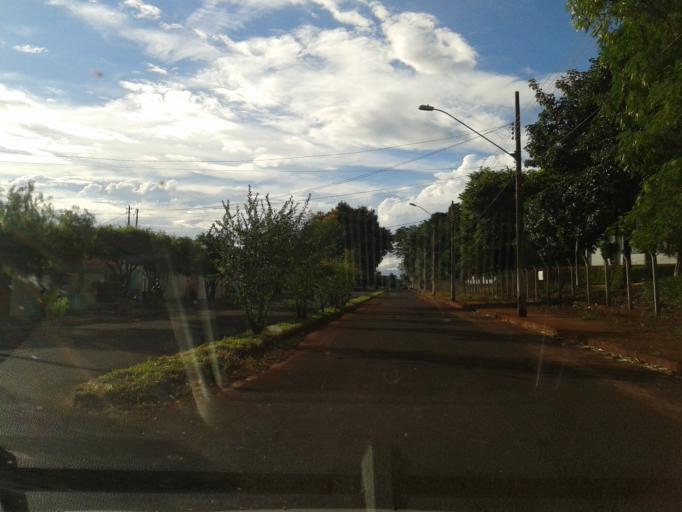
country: BR
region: Minas Gerais
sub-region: Ituiutaba
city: Ituiutaba
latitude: -18.9742
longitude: -49.4471
